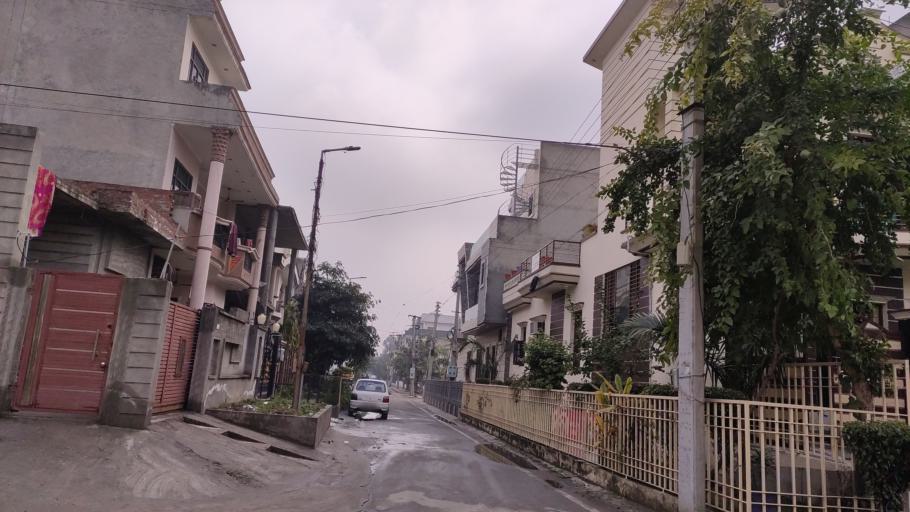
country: IN
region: Punjab
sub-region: Amritsar
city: Amritsar
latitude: 31.6155
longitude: 74.9206
